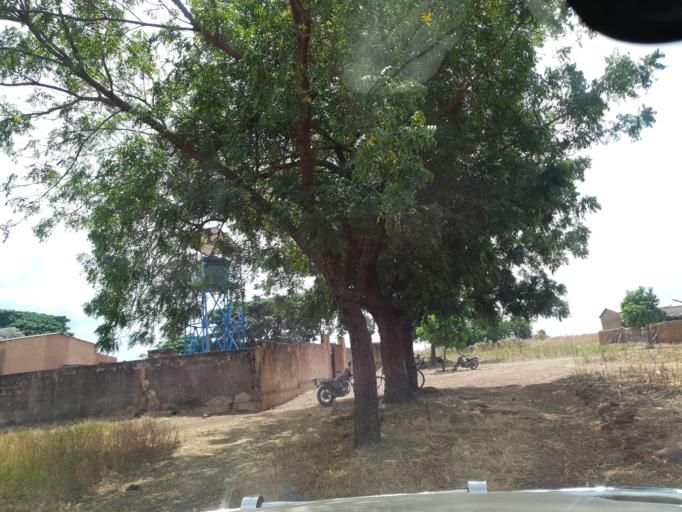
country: ML
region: Sikasso
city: Sikasso
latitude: 11.6741
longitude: -6.1666
